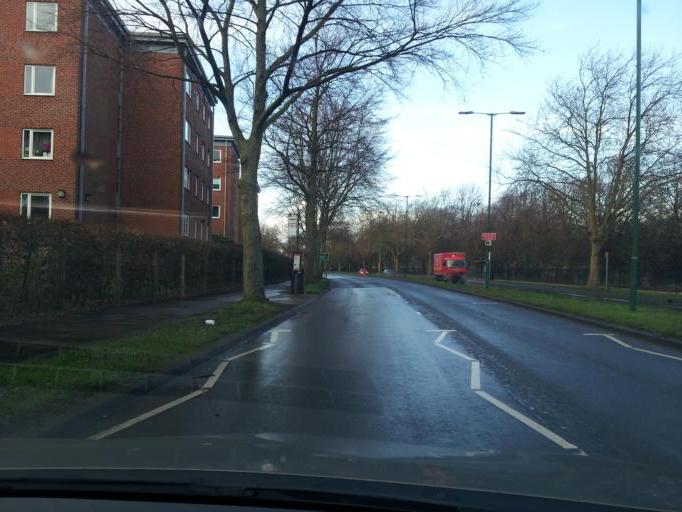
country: GB
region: England
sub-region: Nottingham
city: Nottingham
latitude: 52.9340
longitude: -1.2055
